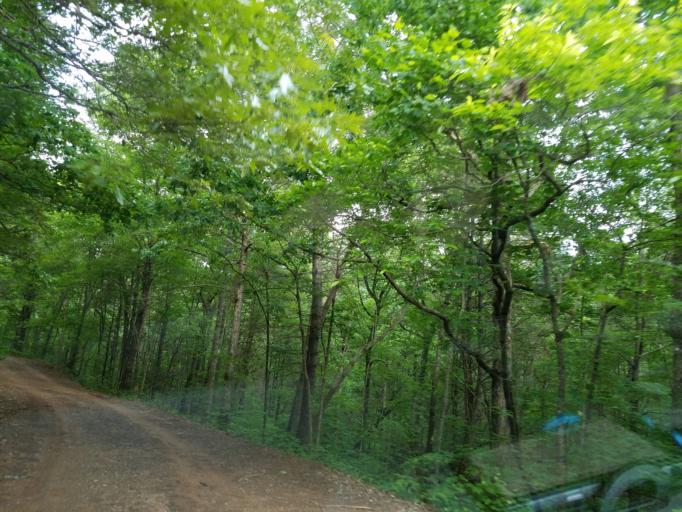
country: US
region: Georgia
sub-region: Lumpkin County
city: Dahlonega
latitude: 34.6002
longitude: -84.1092
